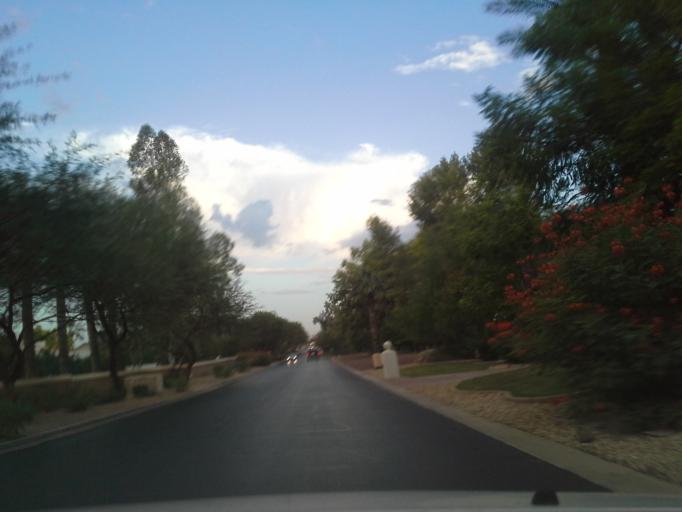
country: US
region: Arizona
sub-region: Maricopa County
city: Paradise Valley
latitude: 33.5342
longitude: -111.9432
